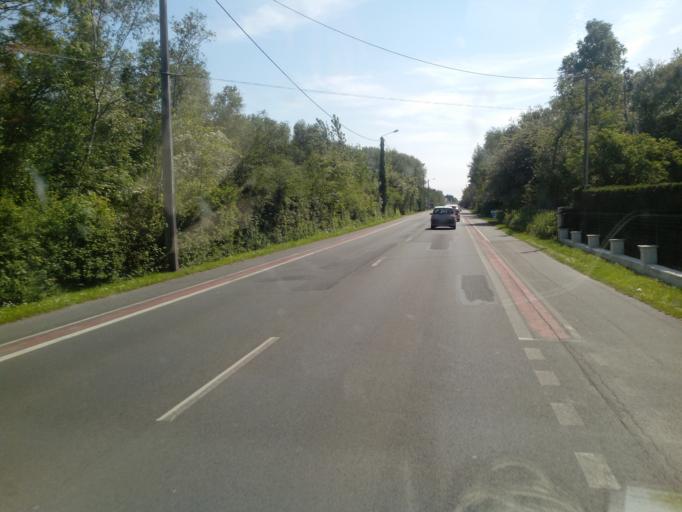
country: FR
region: Nord-Pas-de-Calais
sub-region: Departement du Pas-de-Calais
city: Merlimont
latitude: 50.4365
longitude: 1.6104
